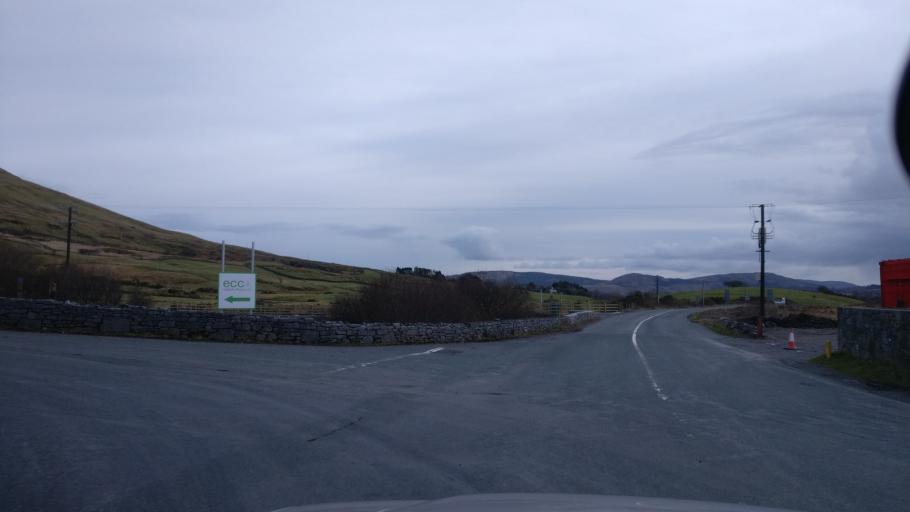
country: IE
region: Connaught
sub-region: County Galway
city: Oughterard
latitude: 53.5403
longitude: -9.4559
